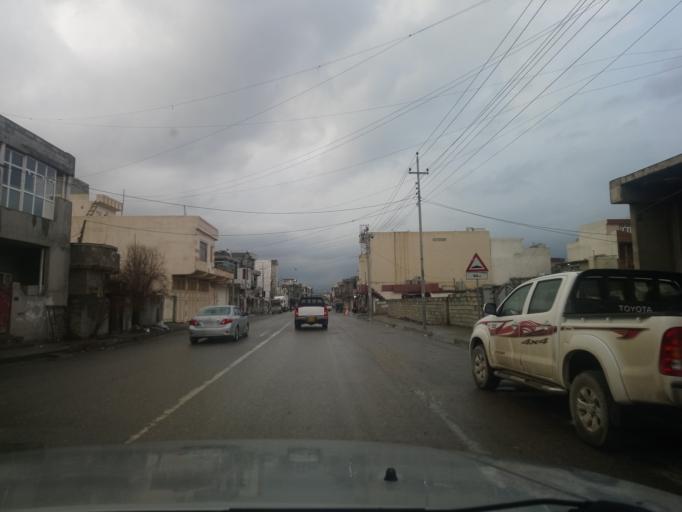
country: IQ
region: As Sulaymaniyah
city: Qeladize
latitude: 36.1834
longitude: 45.1336
